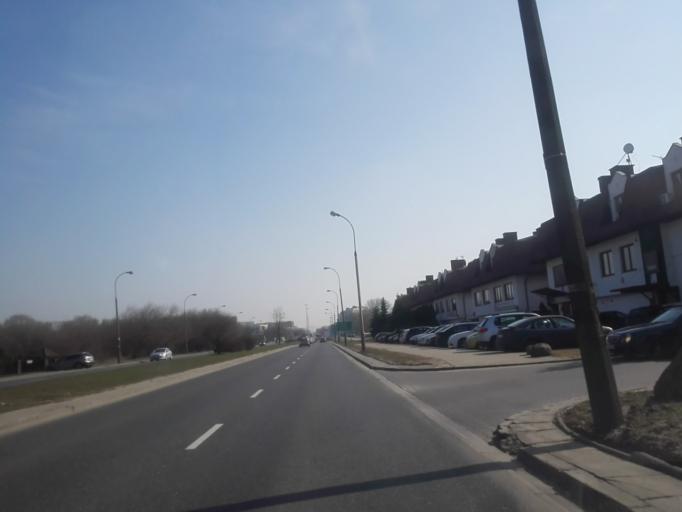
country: PL
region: Masovian Voivodeship
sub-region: Warszawa
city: Mokotow
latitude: 52.1765
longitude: 21.0381
